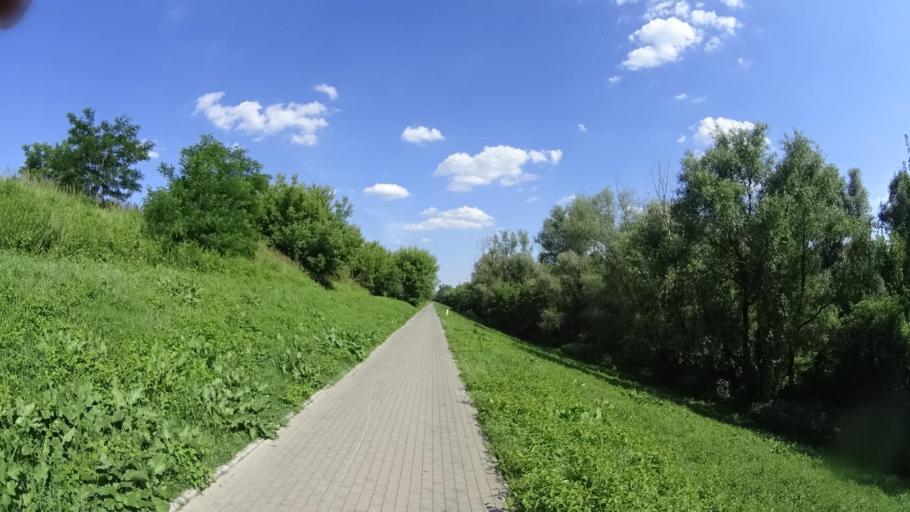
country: PL
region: Masovian Voivodeship
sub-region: Warszawa
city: Bialoleka
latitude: 52.3040
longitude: 20.9627
